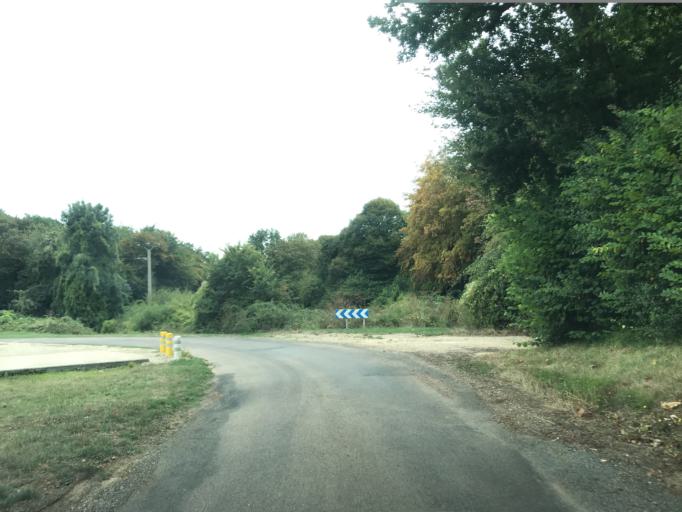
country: FR
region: Haute-Normandie
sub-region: Departement de l'Eure
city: Houlbec-Cocherel
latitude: 49.0641
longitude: 1.3359
